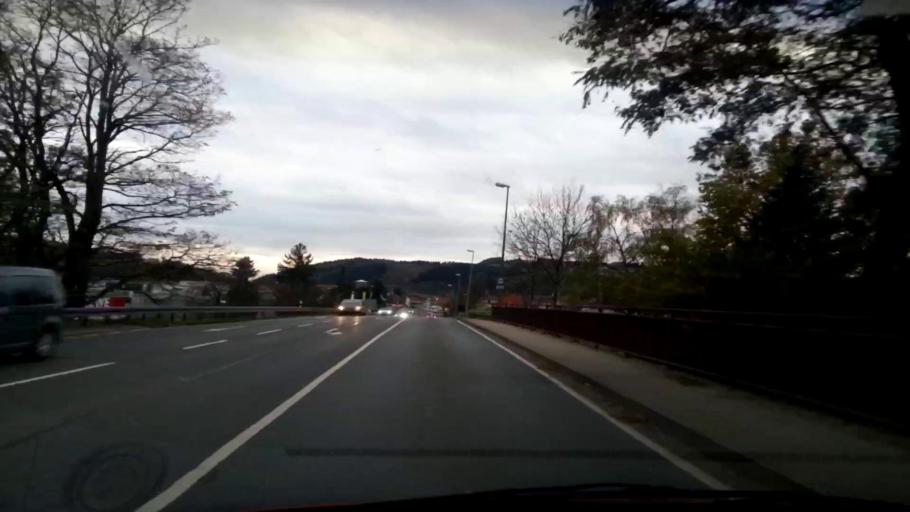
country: DE
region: Bavaria
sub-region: Upper Franconia
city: Kronach
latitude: 50.2341
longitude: 11.3294
